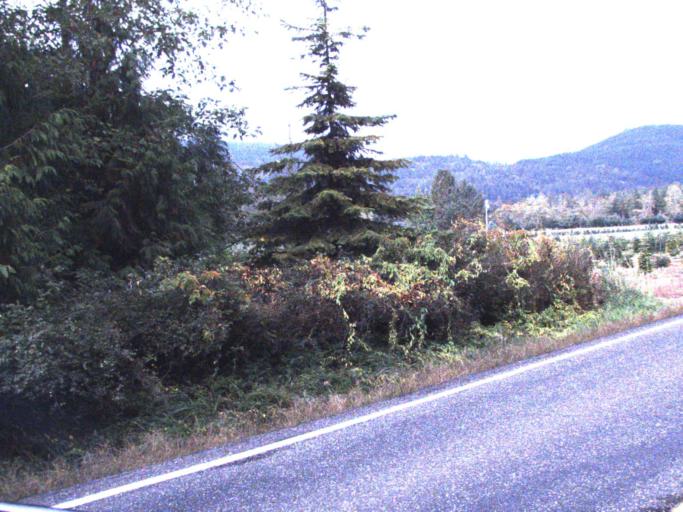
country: US
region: Washington
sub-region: Whatcom County
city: Sudden Valley
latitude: 48.7683
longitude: -122.2017
